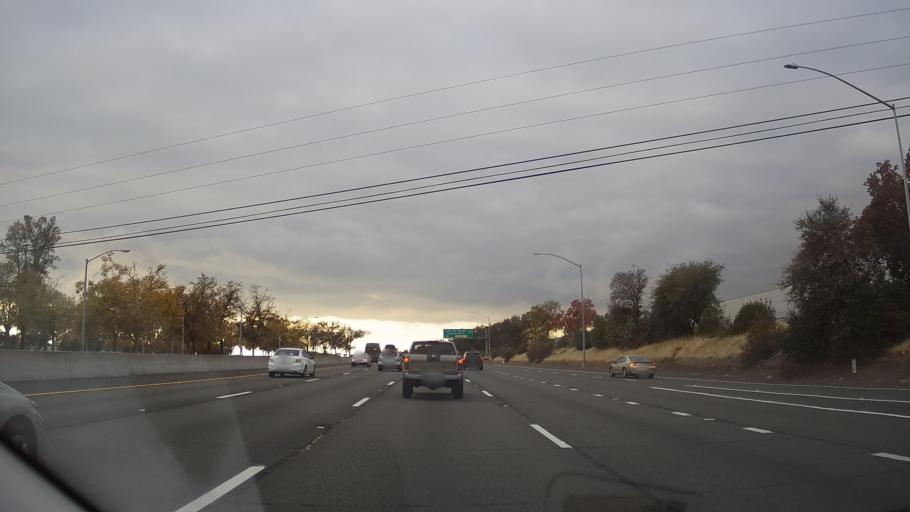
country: US
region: California
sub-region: Sacramento County
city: North Highlands
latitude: 38.6451
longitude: -121.3871
